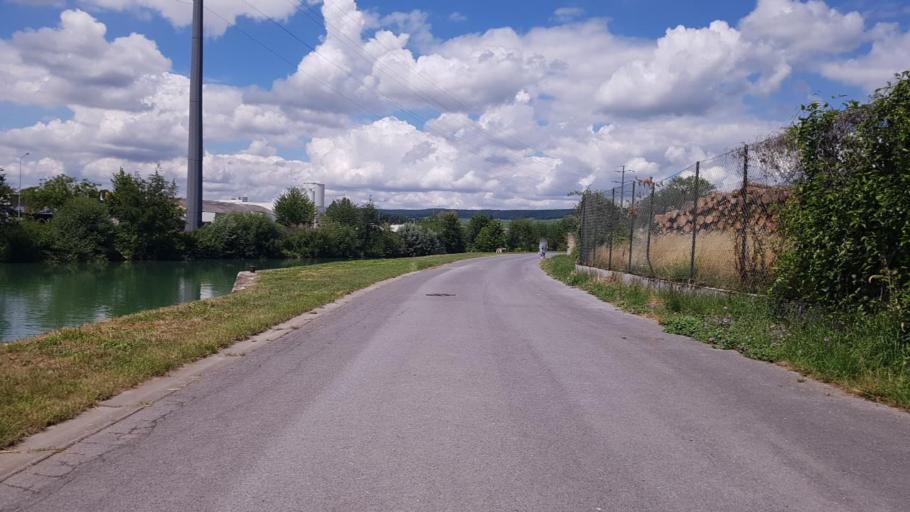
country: FR
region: Champagne-Ardenne
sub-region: Departement de la Marne
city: Magenta
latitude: 49.0514
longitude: 3.9628
